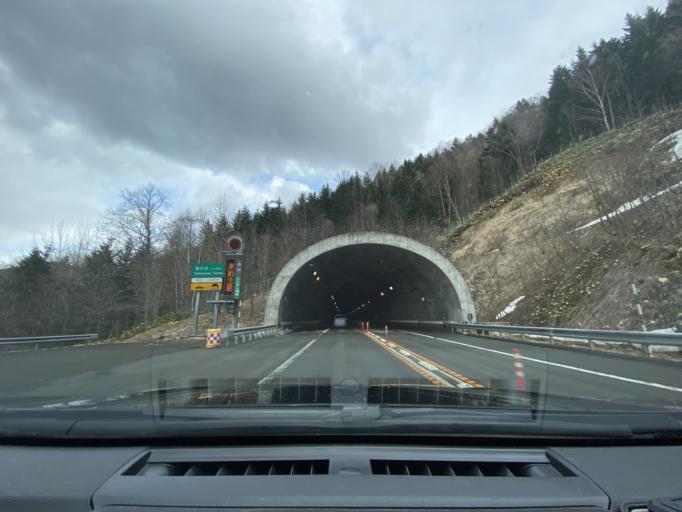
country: JP
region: Hokkaido
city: Shimo-furano
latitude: 43.0463
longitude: 142.4835
